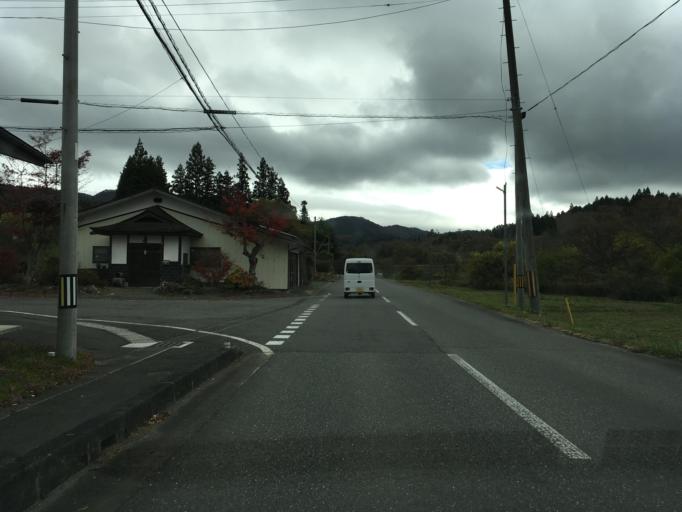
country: JP
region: Iwate
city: Mizusawa
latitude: 39.0650
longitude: 141.3827
